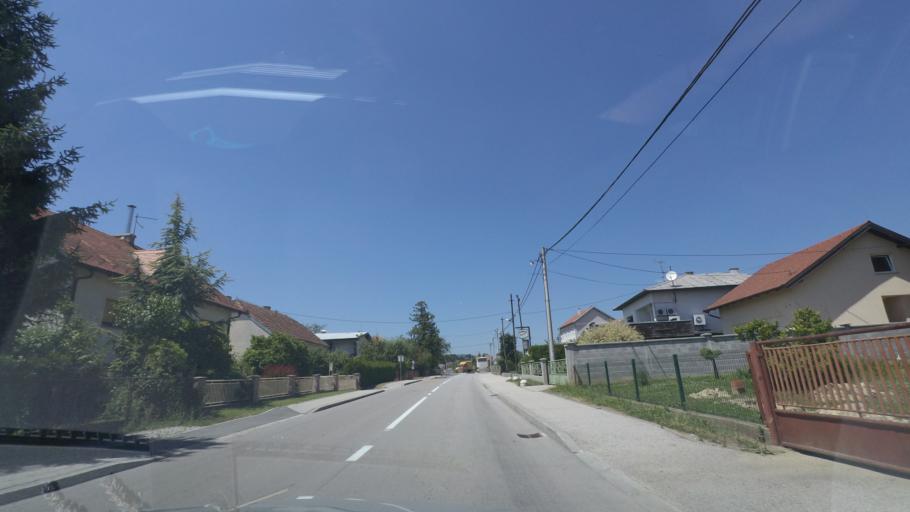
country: HR
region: Grad Zagreb
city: Horvati
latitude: 45.6821
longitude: 15.7516
